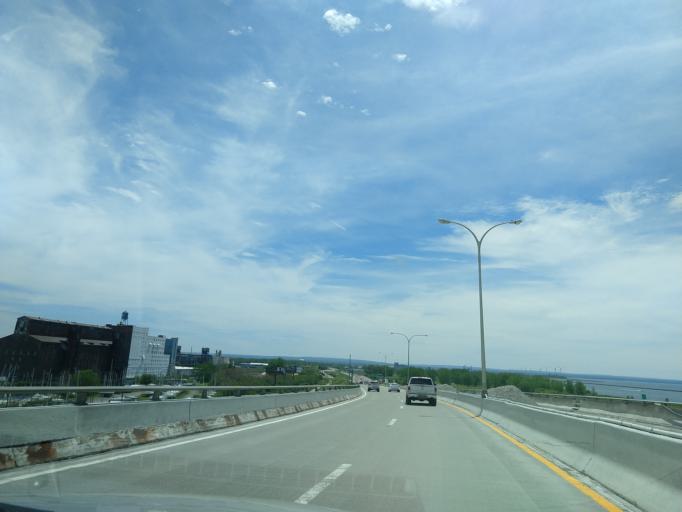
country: US
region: New York
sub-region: Erie County
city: Buffalo
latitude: 42.8697
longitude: -78.8788
